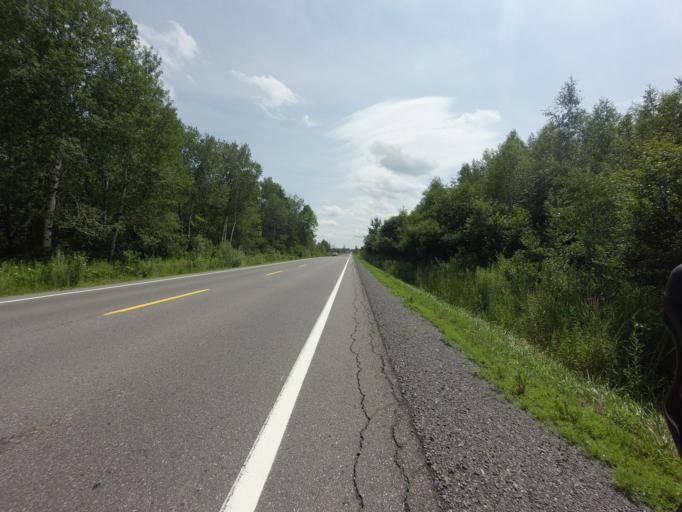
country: CA
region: Ontario
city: Ottawa
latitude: 45.3000
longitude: -75.6398
